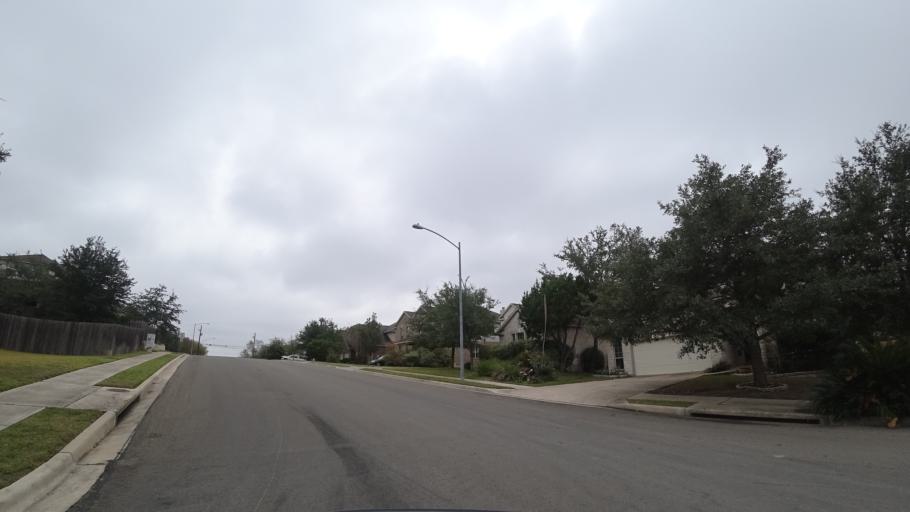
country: US
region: Texas
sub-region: Travis County
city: Barton Creek
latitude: 30.2374
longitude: -97.9025
